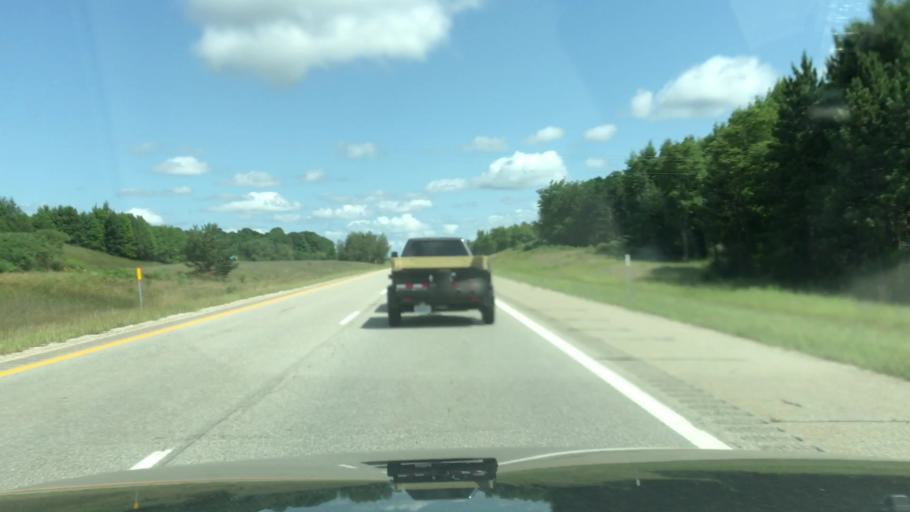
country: US
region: Michigan
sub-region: Mecosta County
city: Big Rapids
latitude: 43.7723
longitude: -85.5344
